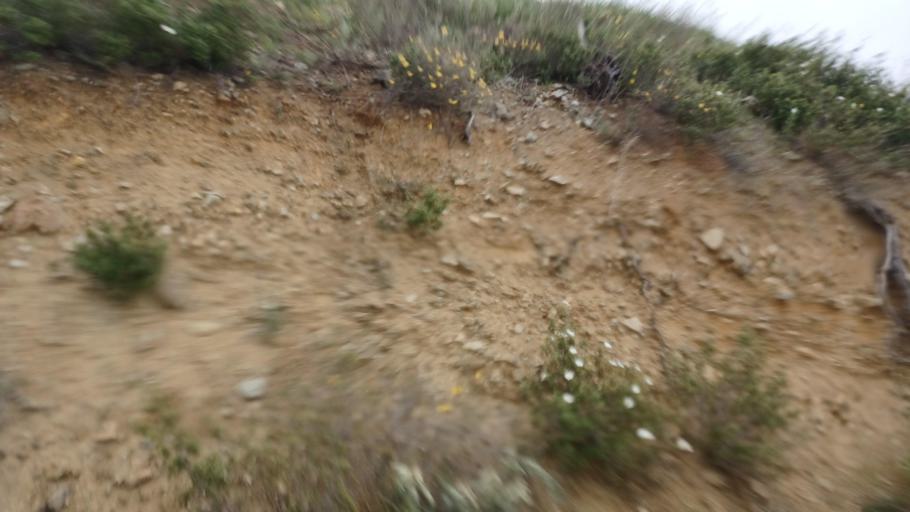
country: CY
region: Limassol
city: Parekklisha
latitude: 34.8505
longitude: 33.1426
